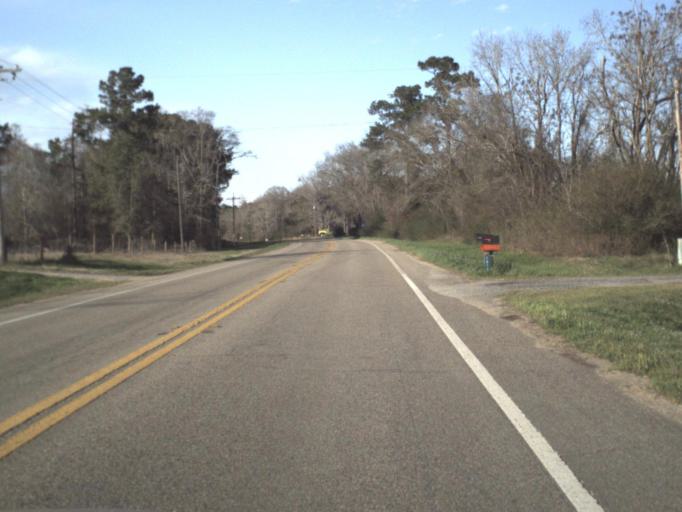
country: US
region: Florida
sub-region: Jackson County
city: Marianna
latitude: 30.7048
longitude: -85.2312
